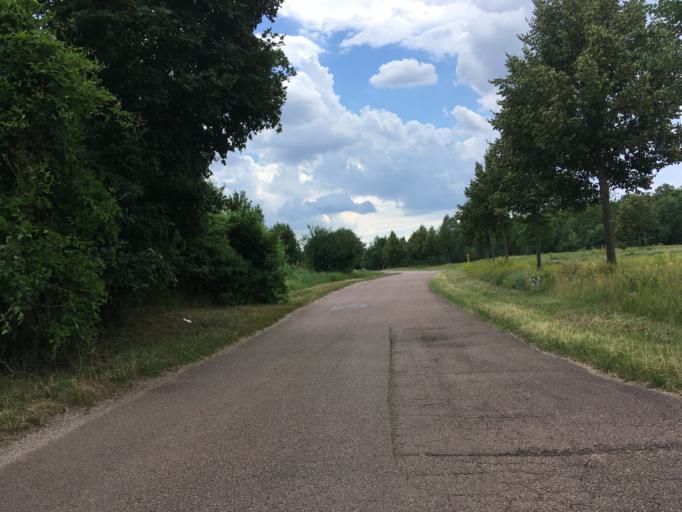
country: DE
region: Saxony-Anhalt
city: Bernburg
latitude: 51.7947
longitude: 11.7623
